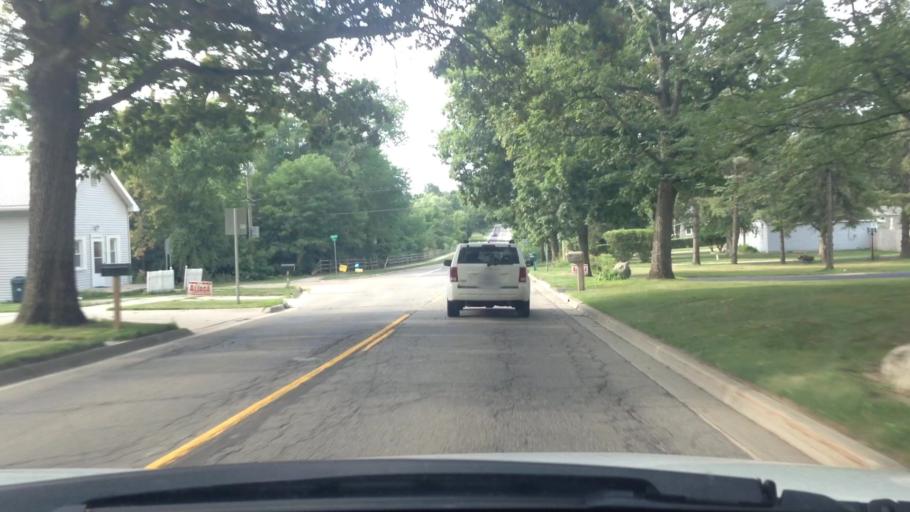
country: US
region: Michigan
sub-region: Oakland County
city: Clarkston
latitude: 42.7508
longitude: -83.3508
